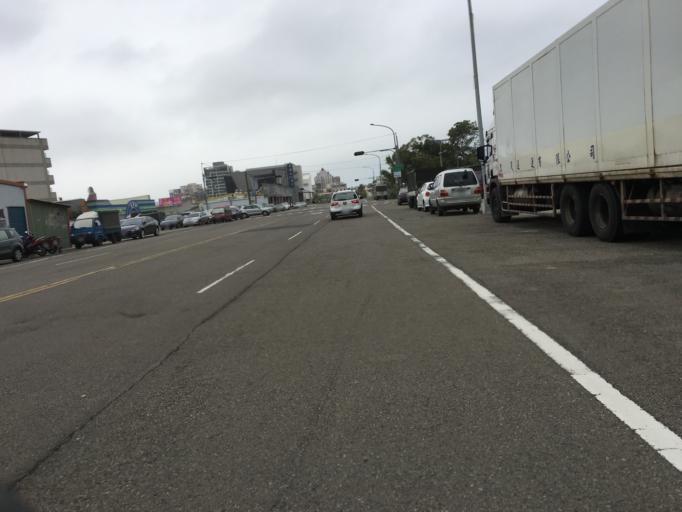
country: TW
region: Taiwan
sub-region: Hsinchu
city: Hsinchu
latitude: 24.6917
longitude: 120.8900
